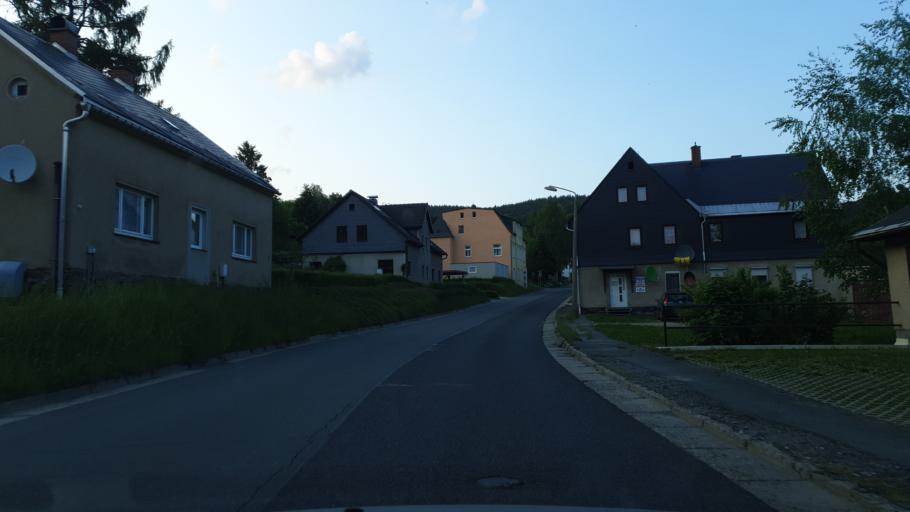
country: DE
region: Saxony
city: Klingenthal
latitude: 50.3784
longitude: 12.4800
